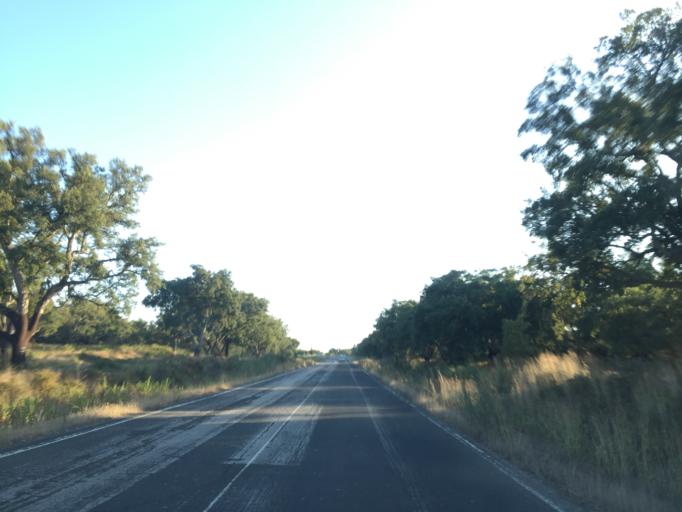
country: PT
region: Santarem
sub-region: Cartaxo
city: Cartaxo
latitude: 39.2064
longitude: -8.7920
